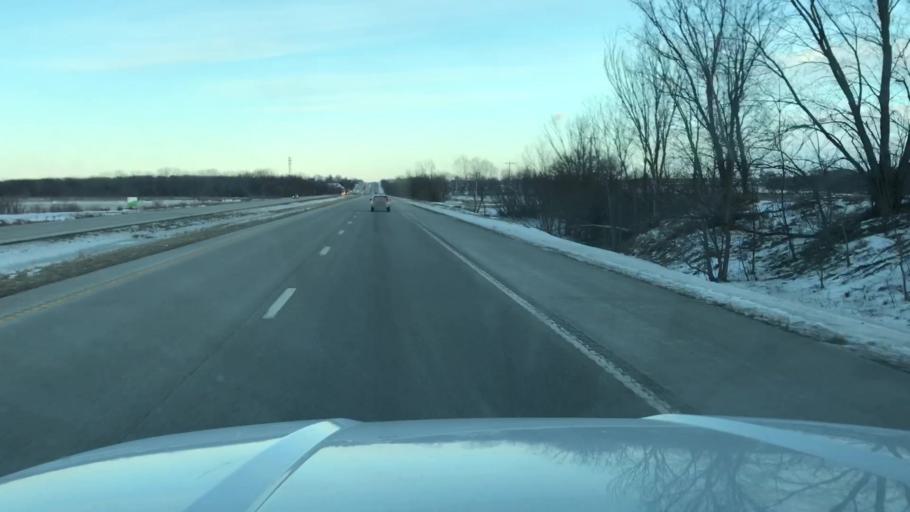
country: US
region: Missouri
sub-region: Clinton County
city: Gower
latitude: 39.7474
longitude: -94.6710
